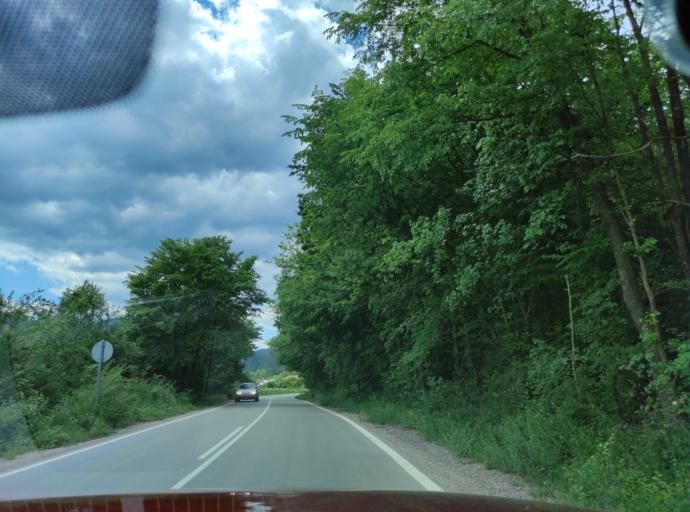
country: BG
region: Montana
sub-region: Obshtina Chiprovtsi
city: Chiprovtsi
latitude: 43.4372
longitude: 22.9463
